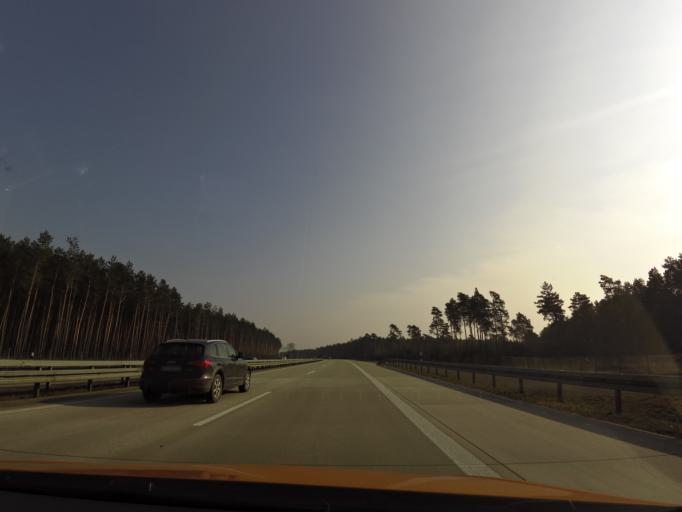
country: DE
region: Brandenburg
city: Briesen
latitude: 52.3252
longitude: 14.2852
